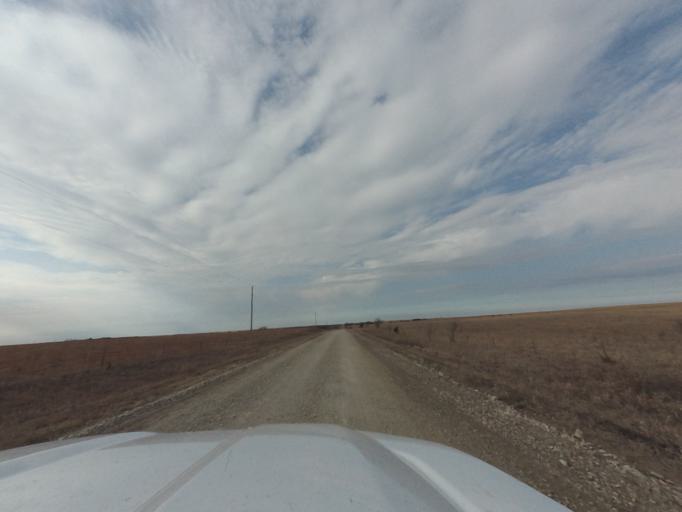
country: US
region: Kansas
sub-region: Chase County
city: Cottonwood Falls
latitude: 38.2170
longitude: -96.6791
